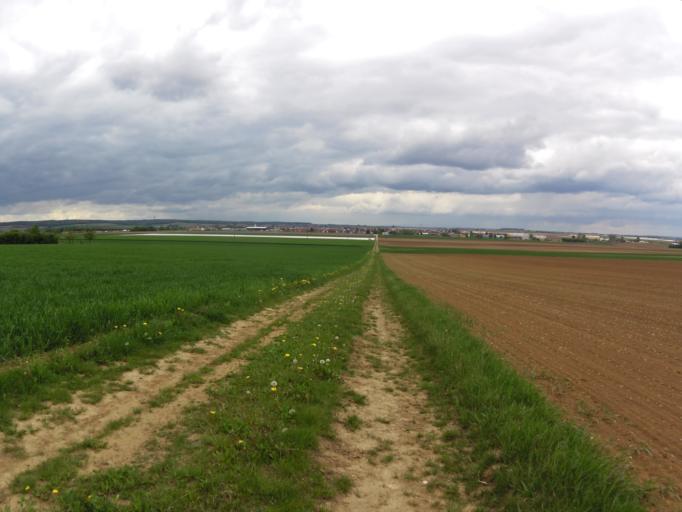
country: DE
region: Bavaria
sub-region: Regierungsbezirk Unterfranken
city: Unterpleichfeld
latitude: 49.8535
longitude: 10.0506
